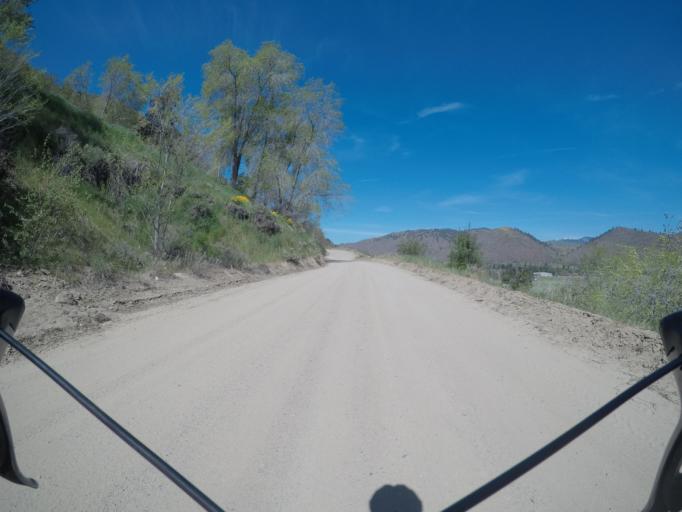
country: US
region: Washington
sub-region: Chelan County
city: Cashmere
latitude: 47.5040
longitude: -120.4446
